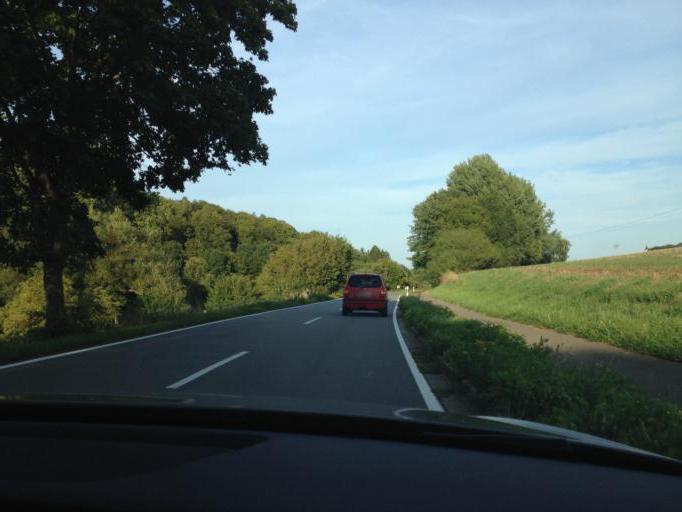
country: DE
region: Rheinland-Pfalz
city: Schonenberg-Kubelberg
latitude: 49.4099
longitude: 7.3490
